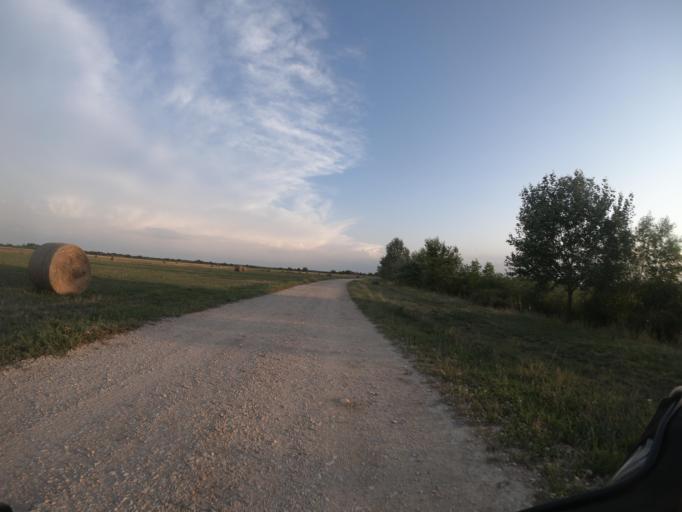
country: HU
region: Jasz-Nagykun-Szolnok
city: Tiszafured
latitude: 47.7266
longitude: 20.7961
